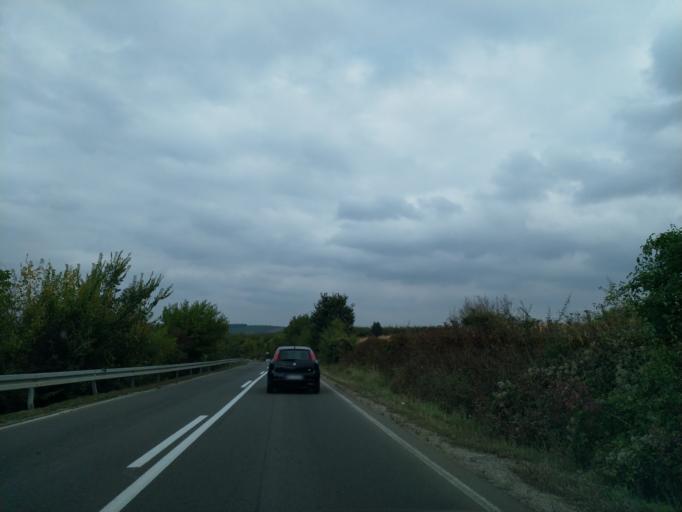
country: RS
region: Central Serbia
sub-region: Sumadijski Okrug
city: Topola
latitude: 44.2056
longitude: 20.7233
